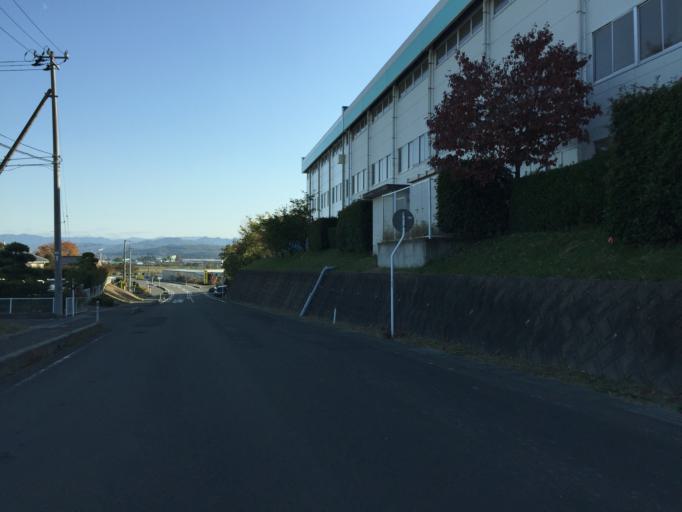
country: JP
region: Fukushima
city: Hobaramachi
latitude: 37.8391
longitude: 140.5079
